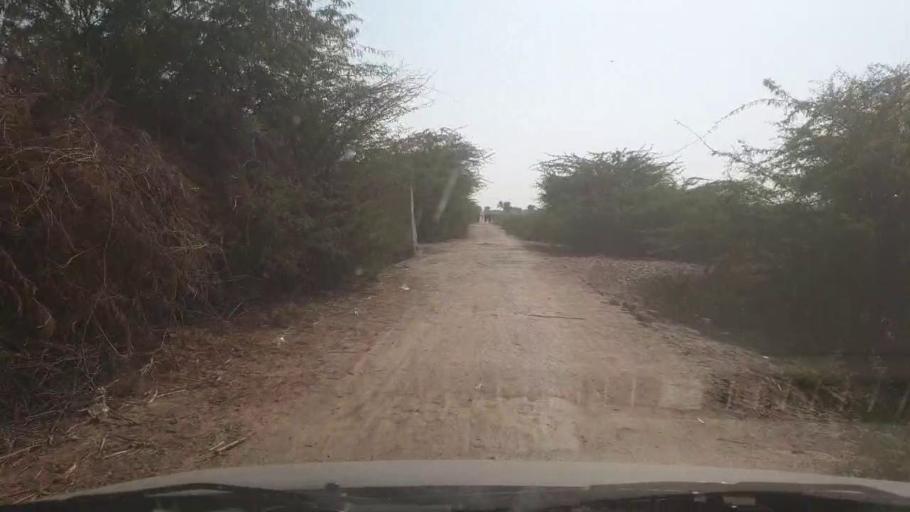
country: PK
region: Sindh
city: Samaro
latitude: 25.1856
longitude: 69.3667
